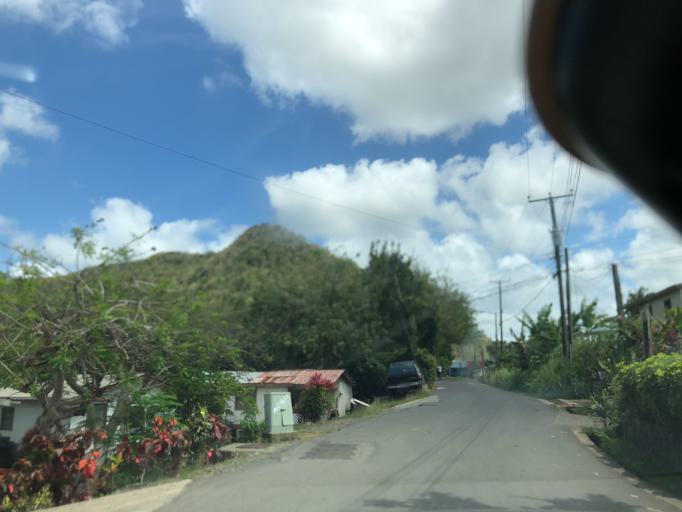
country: LC
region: Gros-Islet
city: Gros Islet
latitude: 14.0560
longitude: -60.9643
